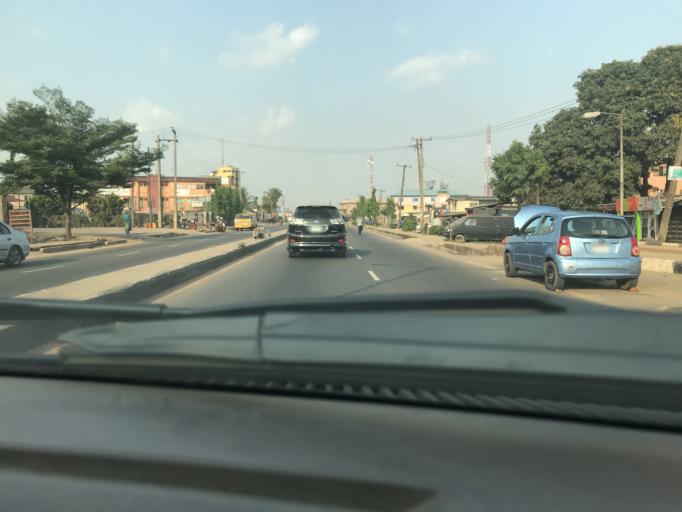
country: NG
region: Lagos
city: Ikotun
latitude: 6.5867
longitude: 3.2857
